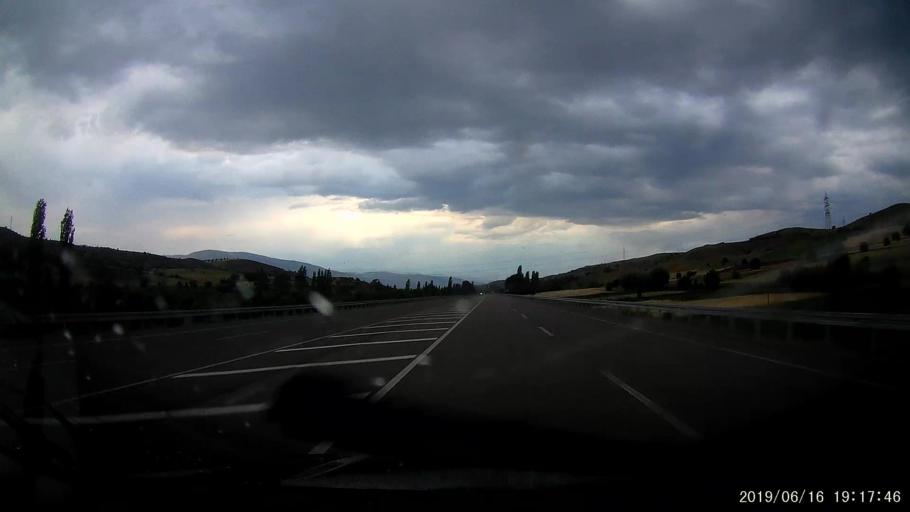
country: TR
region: Sivas
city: Akincilar
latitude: 40.0936
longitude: 38.4768
